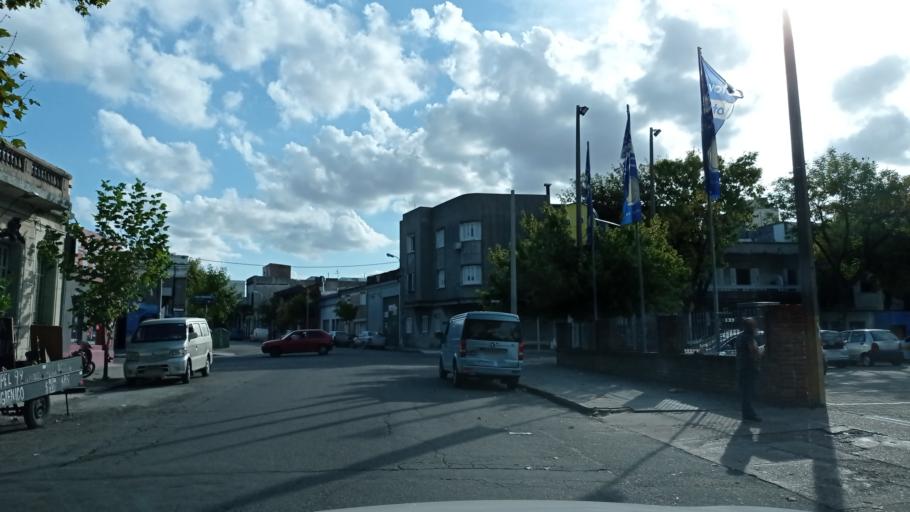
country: UY
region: Montevideo
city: Montevideo
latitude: -34.8929
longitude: -56.1806
